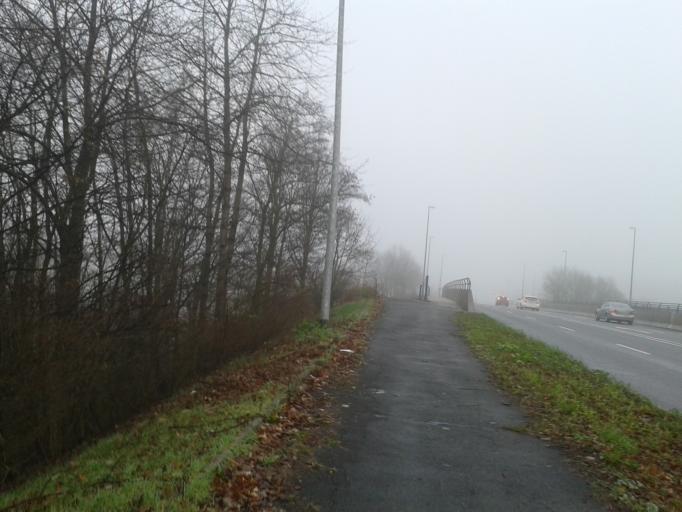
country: DE
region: Bavaria
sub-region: Upper Franconia
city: Bamberg
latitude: 49.9221
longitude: 10.8990
